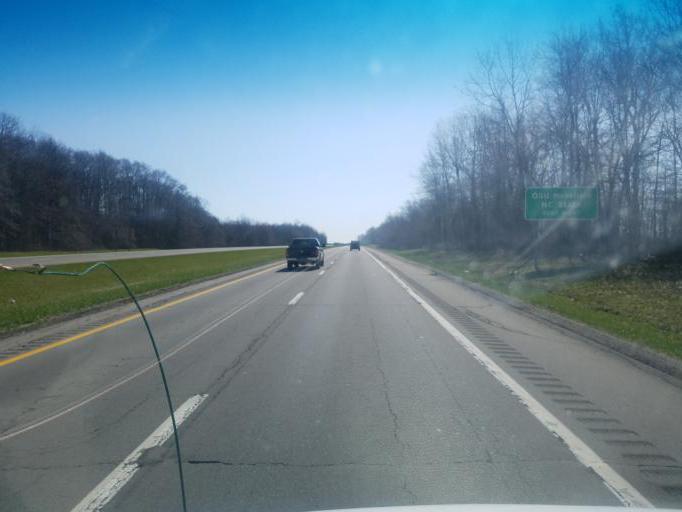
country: US
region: Ohio
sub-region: Richland County
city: Ontario
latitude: 40.7835
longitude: -82.6096
